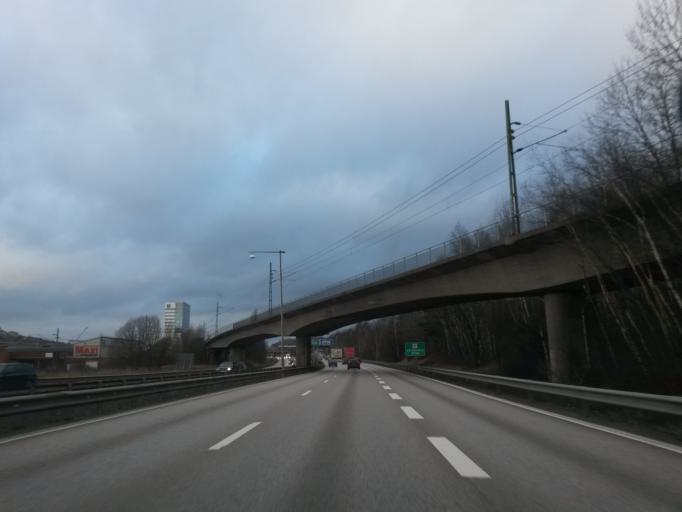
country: SE
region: Vaestra Goetaland
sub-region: Molndal
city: Moelndal
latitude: 57.6784
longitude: 12.0086
